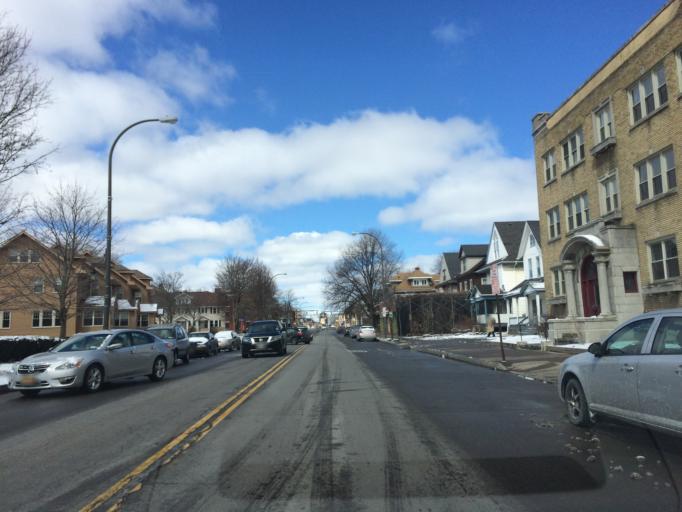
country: US
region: New York
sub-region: Monroe County
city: Brighton
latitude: 43.1405
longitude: -77.5830
